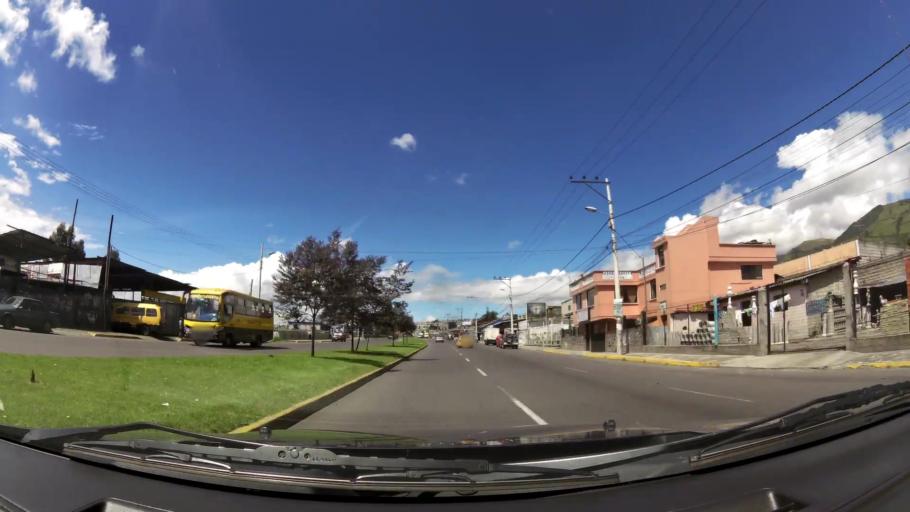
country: EC
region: Pichincha
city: Quito
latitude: -0.3066
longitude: -78.5594
